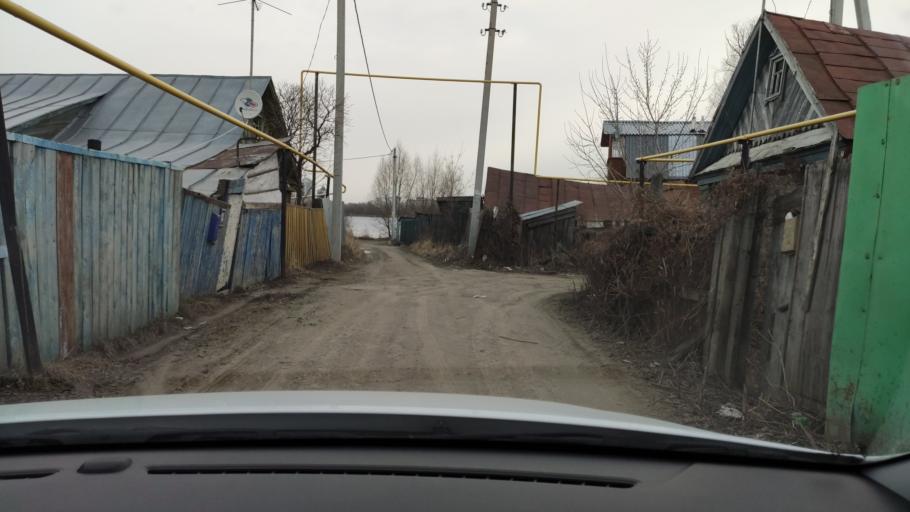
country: RU
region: Tatarstan
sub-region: Gorod Kazan'
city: Kazan
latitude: 55.7446
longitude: 49.1485
